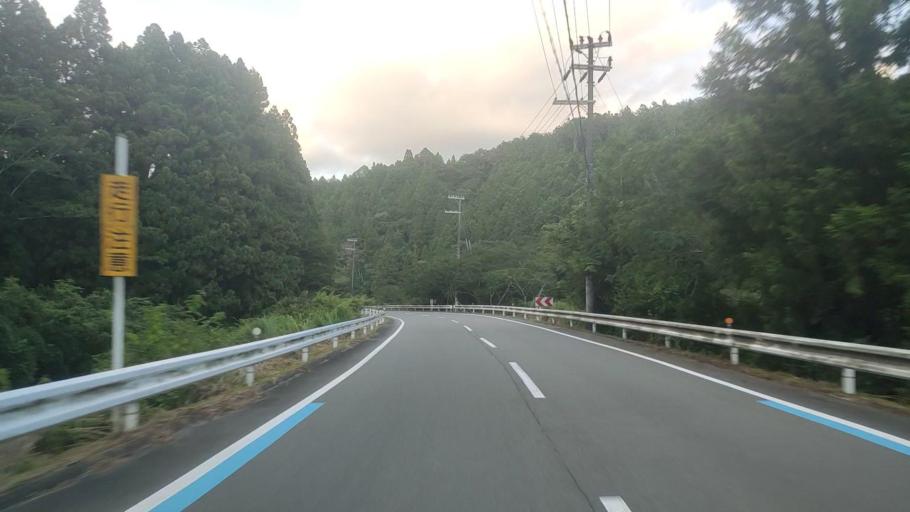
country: JP
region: Wakayama
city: Tanabe
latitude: 33.8252
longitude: 135.6347
